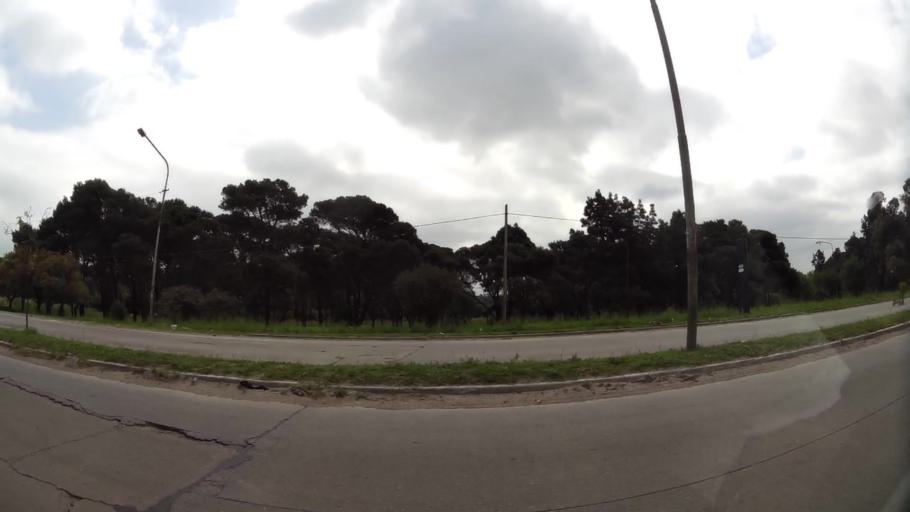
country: AR
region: Buenos Aires
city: San Justo
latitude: -34.7210
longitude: -58.5355
